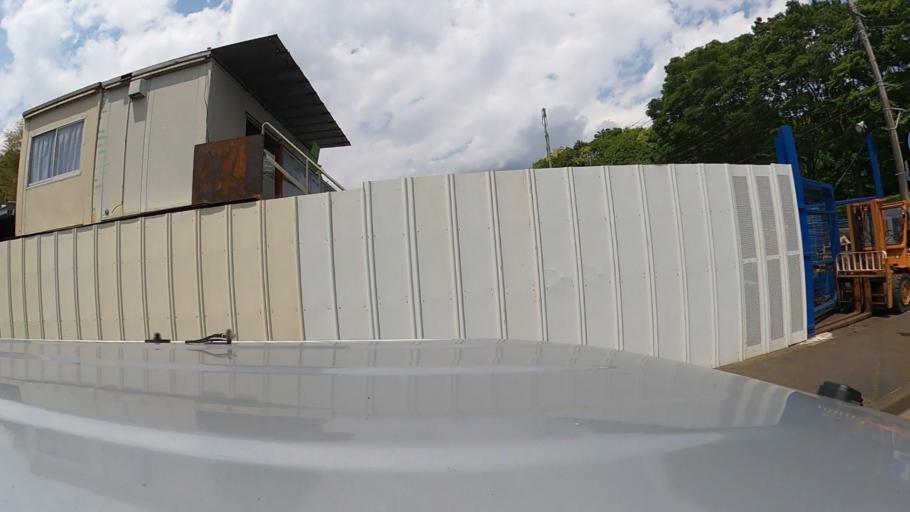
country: JP
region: Kanagawa
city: Fujisawa
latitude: 35.3845
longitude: 139.4249
